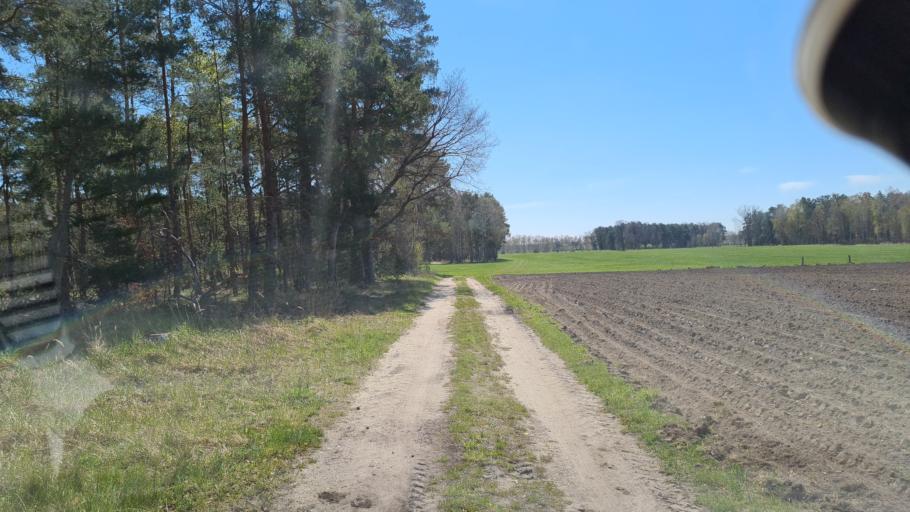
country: DE
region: Brandenburg
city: Ruckersdorf
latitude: 51.5538
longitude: 13.6185
